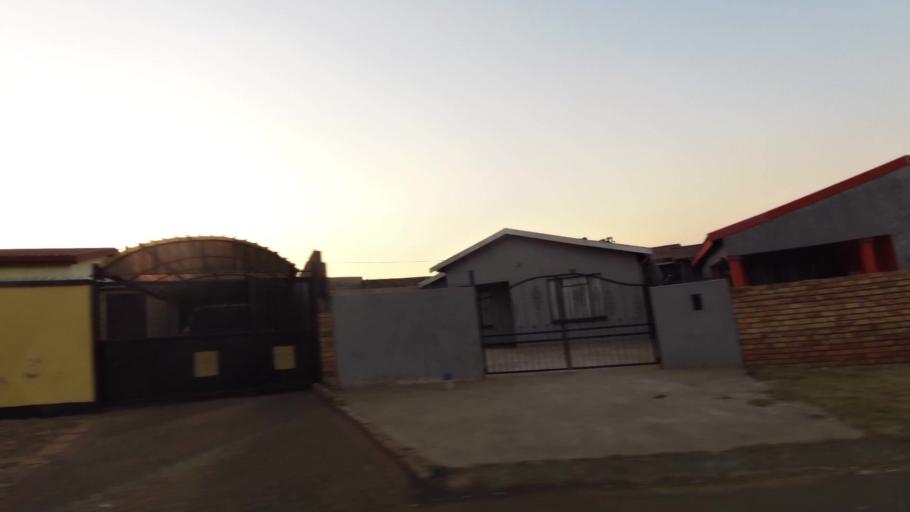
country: ZA
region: Gauteng
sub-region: City of Johannesburg Metropolitan Municipality
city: Soweto
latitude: -26.2845
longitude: 27.8787
